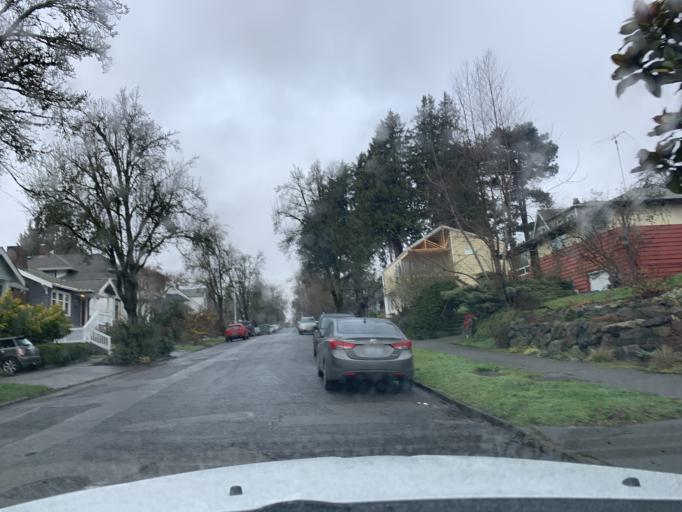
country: US
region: Washington
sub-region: King County
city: Seattle
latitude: 47.6062
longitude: -122.2915
